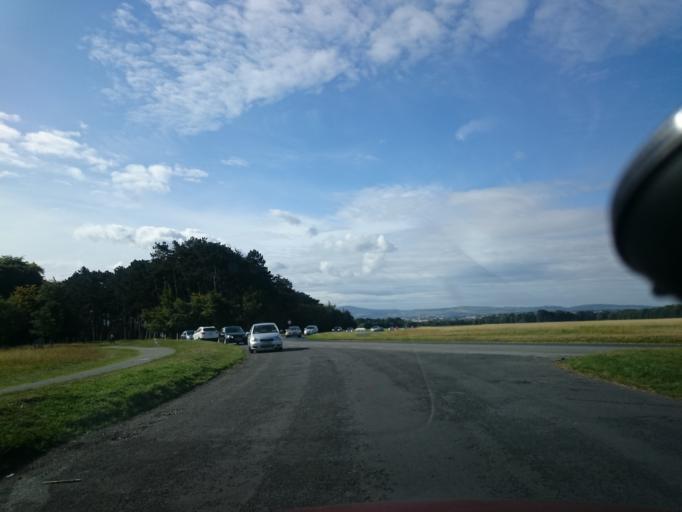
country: IE
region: Leinster
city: Chapelizod
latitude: 53.3566
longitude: -6.3247
